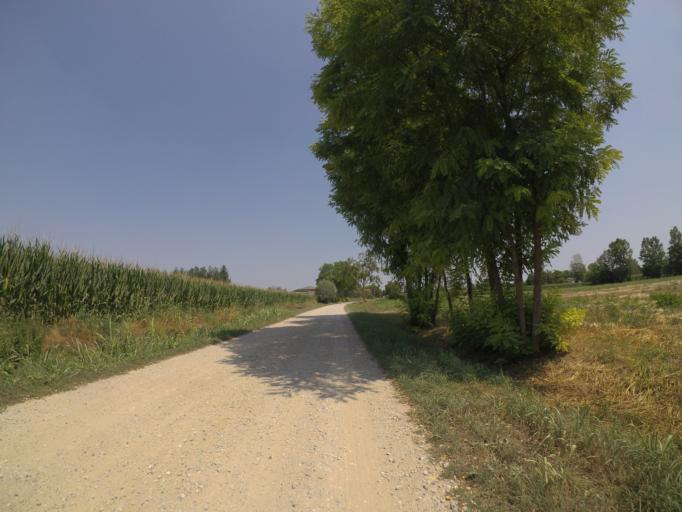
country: IT
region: Friuli Venezia Giulia
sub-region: Provincia di Udine
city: Talmassons
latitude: 45.9179
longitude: 13.1316
